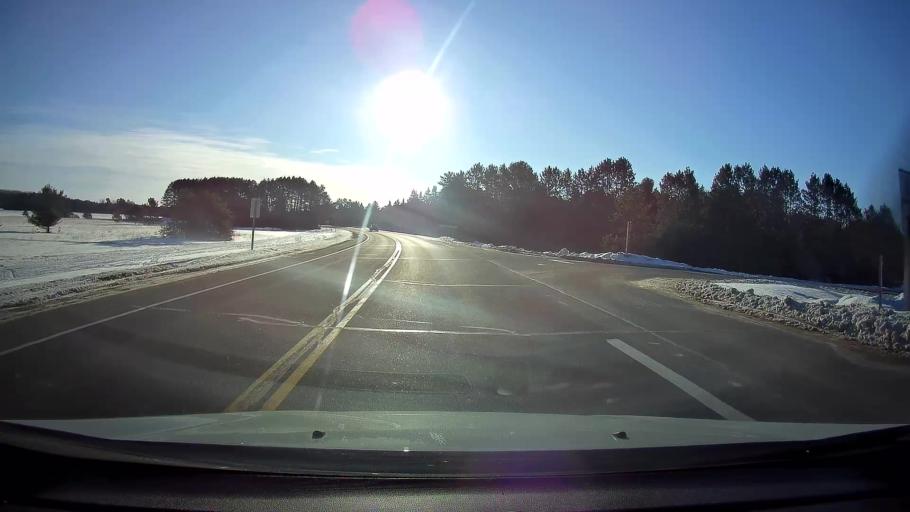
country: US
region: Wisconsin
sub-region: Sawyer County
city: Hayward
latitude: 45.9883
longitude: -91.5914
